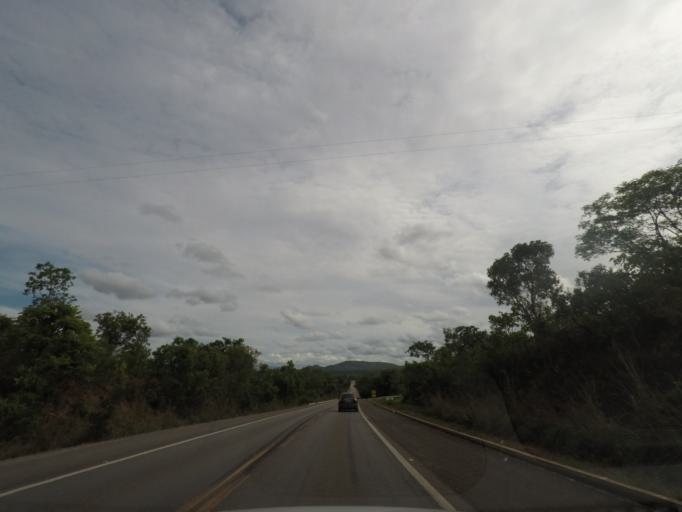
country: BR
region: Goias
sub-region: Uruacu
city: Uruacu
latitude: -14.7366
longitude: -49.0693
